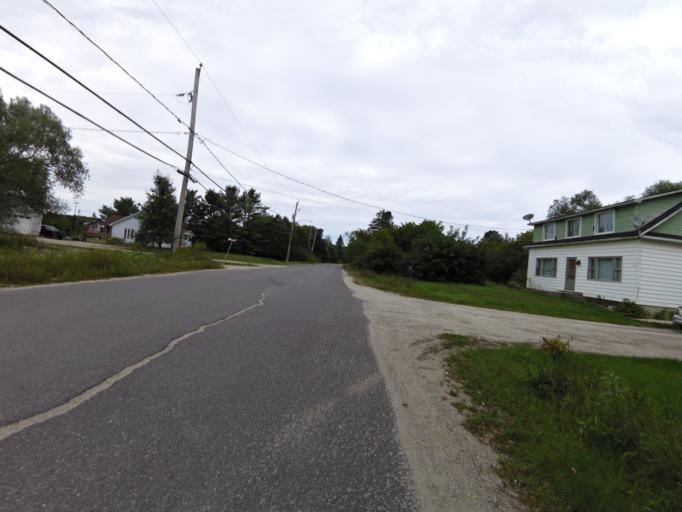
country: CA
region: Quebec
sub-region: Outaouais
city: Wakefield
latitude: 45.8072
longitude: -75.9457
